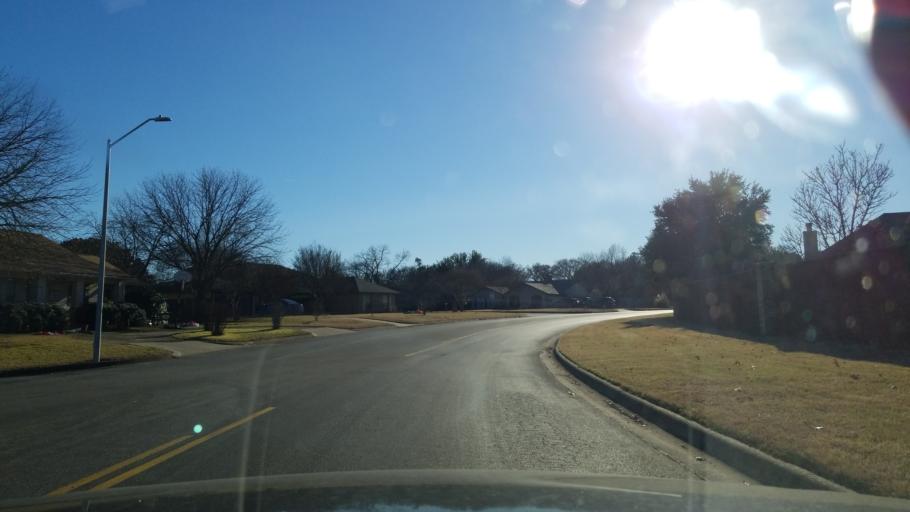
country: US
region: Texas
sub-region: Denton County
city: Corinth
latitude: 33.1565
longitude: -97.0719
